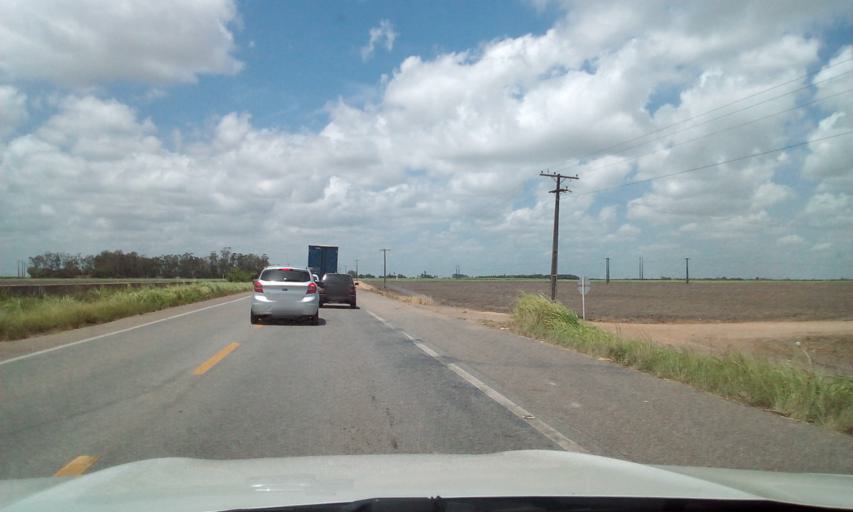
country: BR
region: Alagoas
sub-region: Campo Alegre
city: Campo Alegre
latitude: -9.9033
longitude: -36.2279
